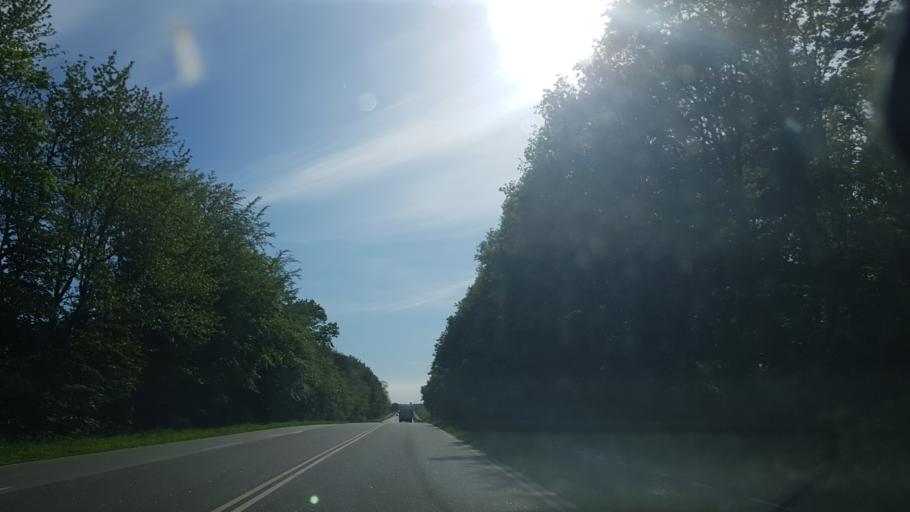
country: DK
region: Zealand
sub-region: Soro Kommune
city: Soro
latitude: 55.4345
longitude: 11.4916
